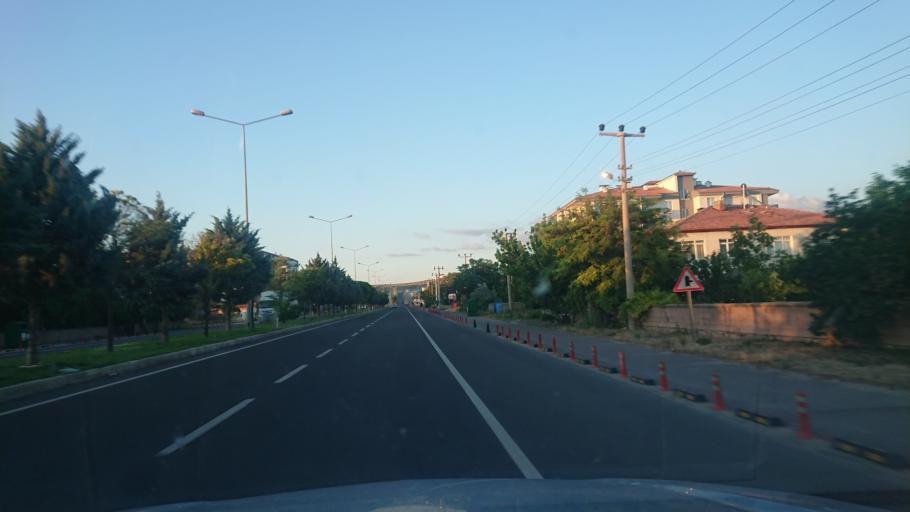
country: TR
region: Aksaray
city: Aksaray
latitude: 38.3943
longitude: 34.0085
